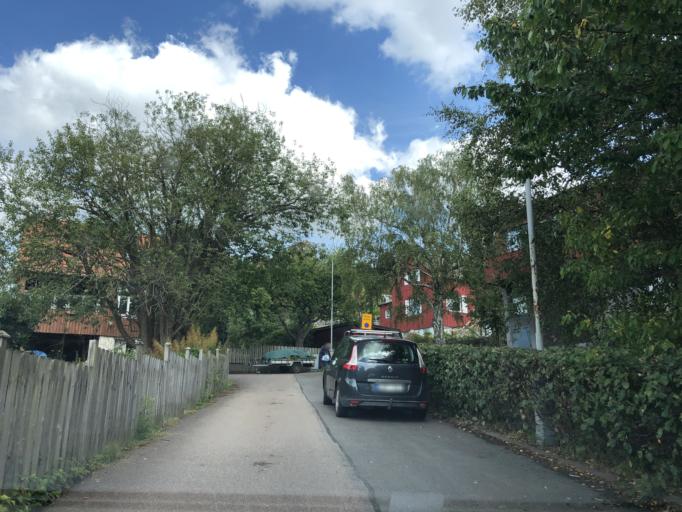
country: SE
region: Vaestra Goetaland
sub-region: Goteborg
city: Majorna
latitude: 57.7229
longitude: 11.9107
